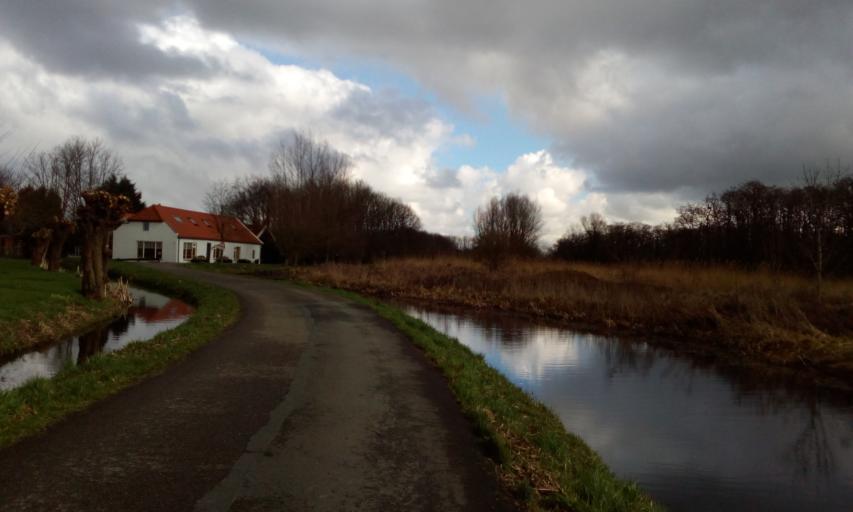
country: NL
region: South Holland
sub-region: Gemeente Pijnacker-Nootdorp
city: Pijnacker
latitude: 51.9789
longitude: 4.4039
